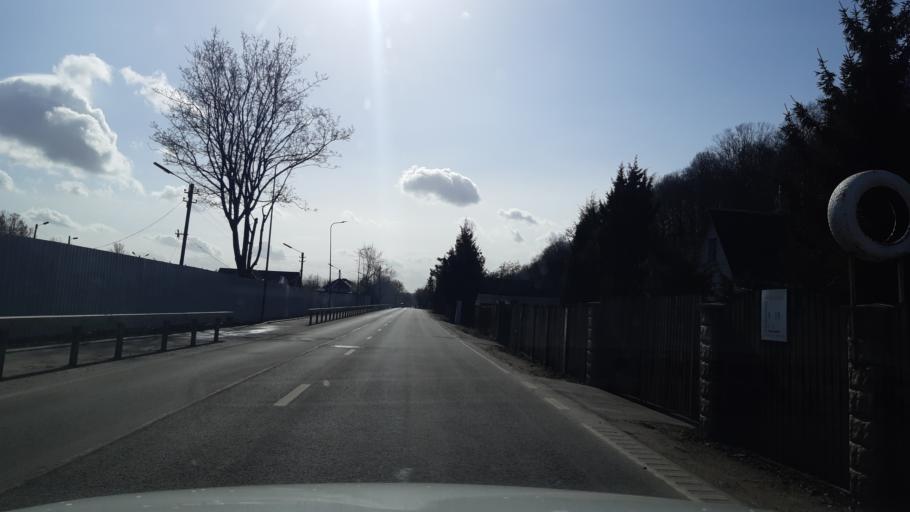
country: LT
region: Kauno apskritis
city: Dainava (Kaunas)
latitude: 54.8804
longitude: 23.9573
